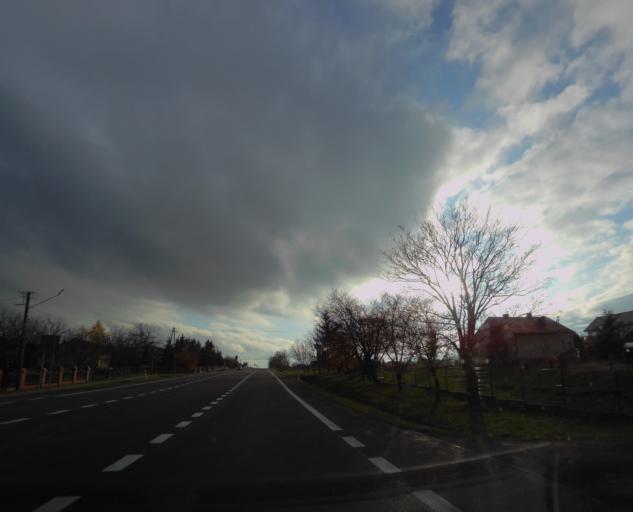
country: PL
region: Subcarpathian Voivodeship
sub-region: Powiat przemyski
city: Orly
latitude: 49.8845
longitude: 22.8153
